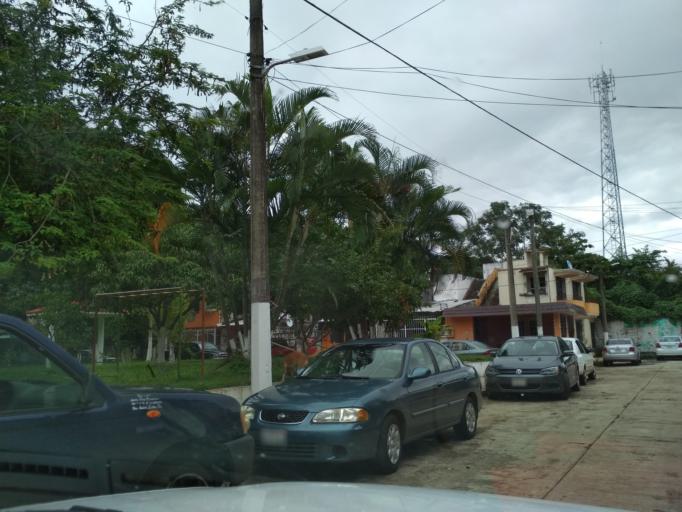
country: MX
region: Veracruz
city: San Andres Tuxtla
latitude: 18.4482
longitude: -95.2286
